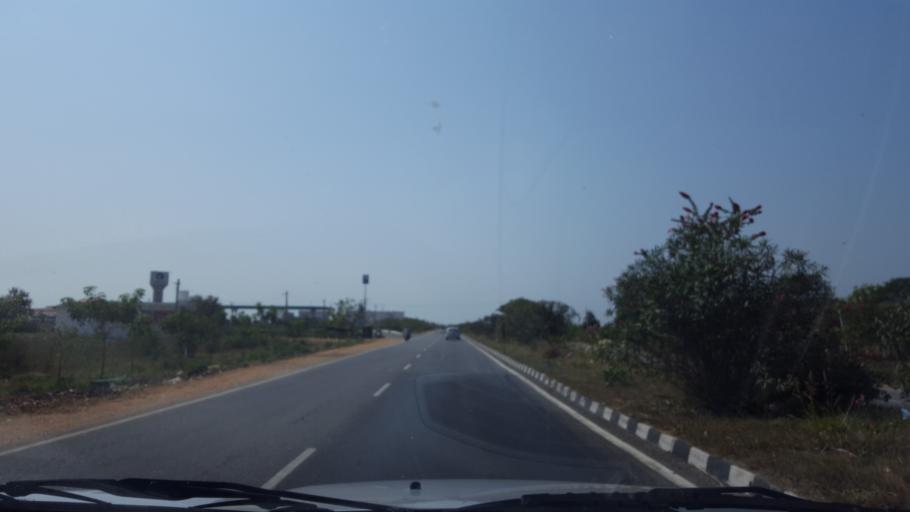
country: IN
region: Andhra Pradesh
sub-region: Guntur
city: Chilakalurupet
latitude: 16.0740
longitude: 80.1553
